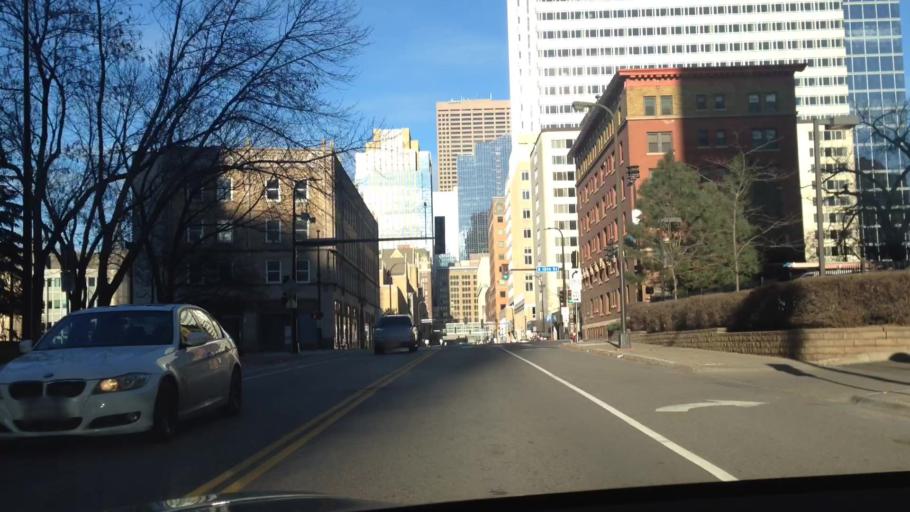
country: US
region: Minnesota
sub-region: Hennepin County
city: Minneapolis
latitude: 44.9722
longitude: -93.2783
